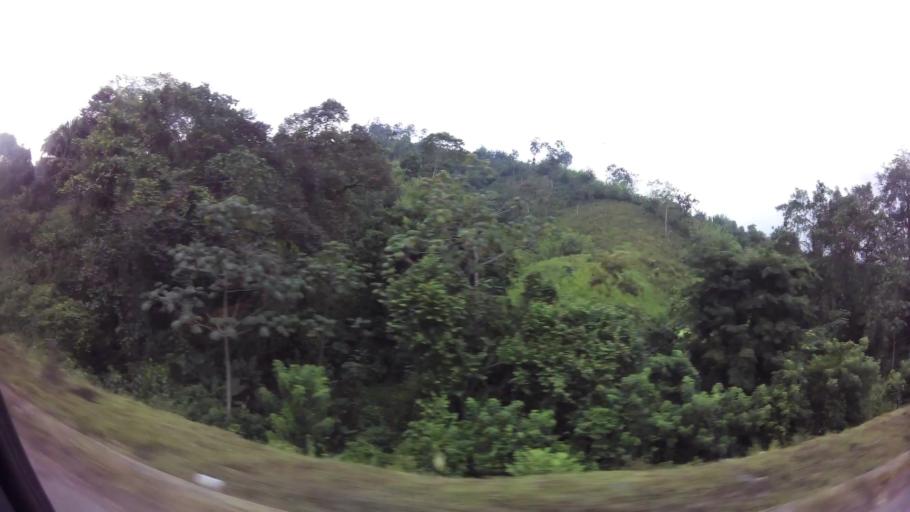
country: HN
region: Yoro
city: Guaimitas
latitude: 15.5049
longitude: -87.6969
